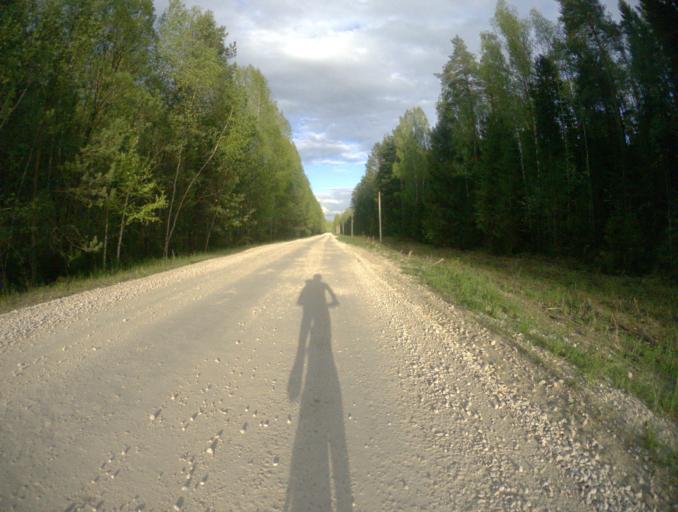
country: RU
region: Vladimir
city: Anopino
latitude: 55.7190
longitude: 40.6154
